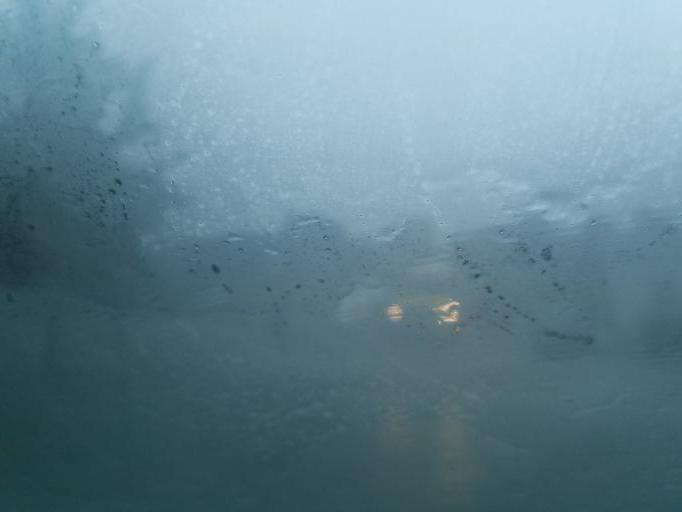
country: US
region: Ohio
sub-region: Williams County
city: Edgerton
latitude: 41.4483
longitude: -84.7413
